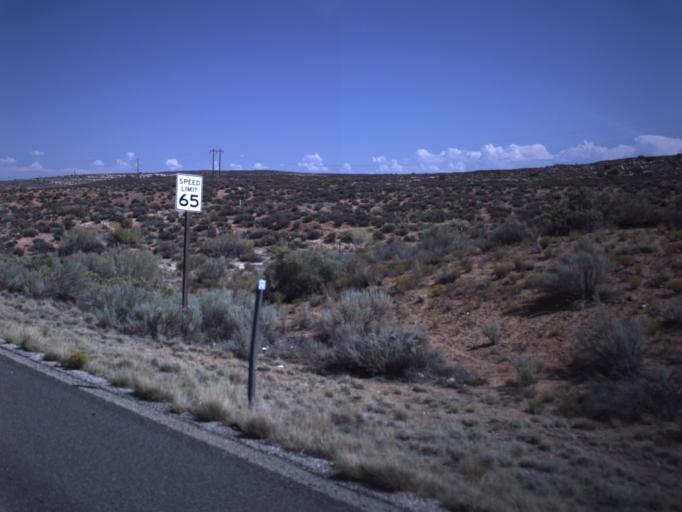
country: US
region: Utah
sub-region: San Juan County
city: Blanding
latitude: 37.3542
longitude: -109.5180
